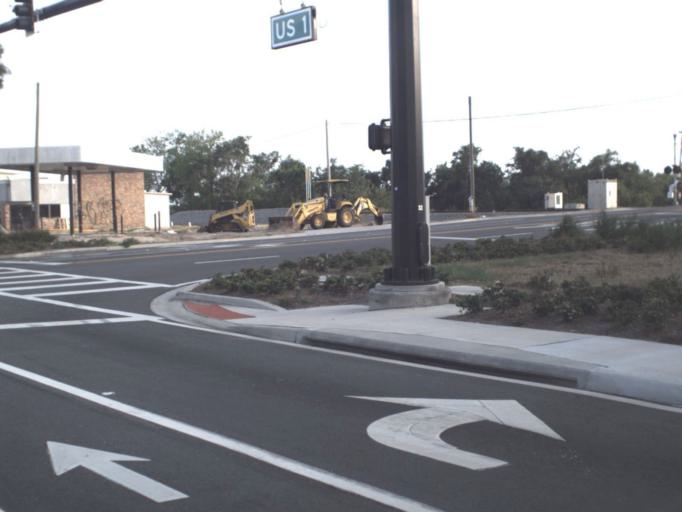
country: US
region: Florida
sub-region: Brevard County
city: Cocoa
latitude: 28.3903
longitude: -80.7467
